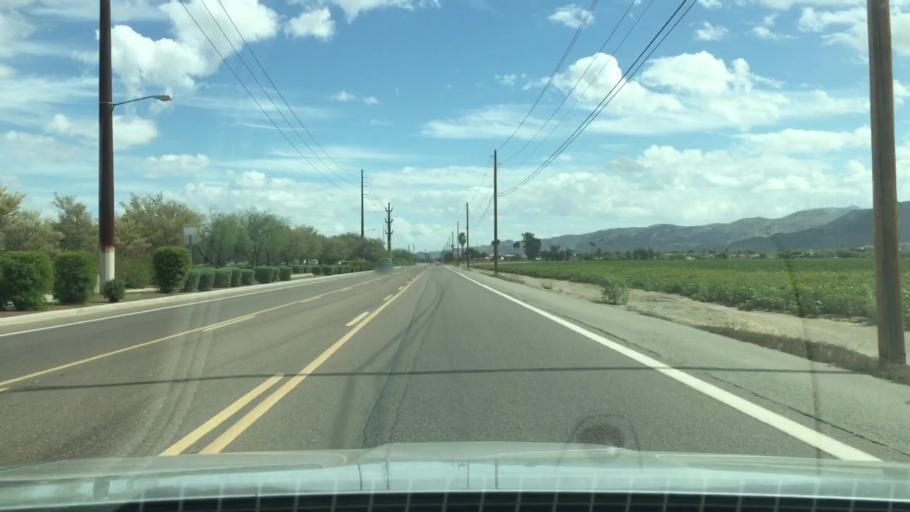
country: US
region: Arizona
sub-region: Maricopa County
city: Laveen
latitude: 33.3630
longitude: -112.1485
